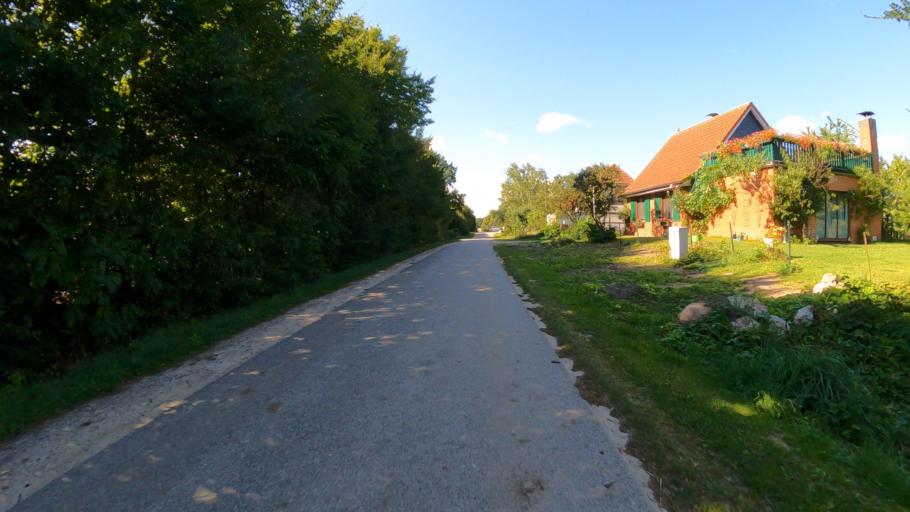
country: DE
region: Schleswig-Holstein
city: Gross Boden
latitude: 53.7478
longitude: 10.4611
